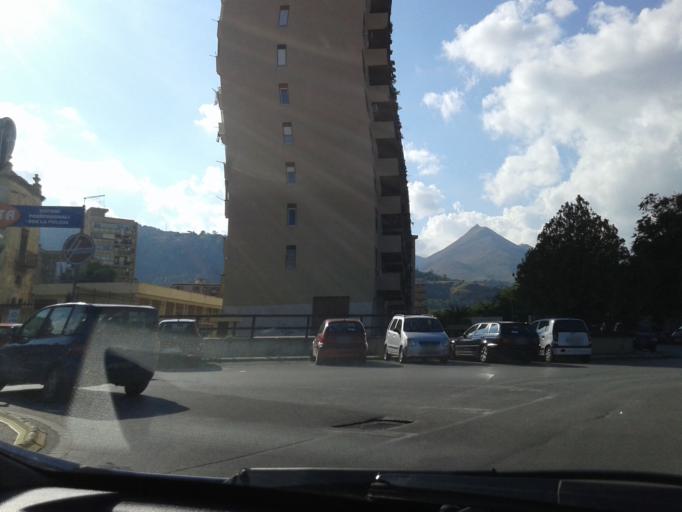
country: IT
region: Sicily
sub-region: Palermo
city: Palermo
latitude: 38.1031
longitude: 13.3241
